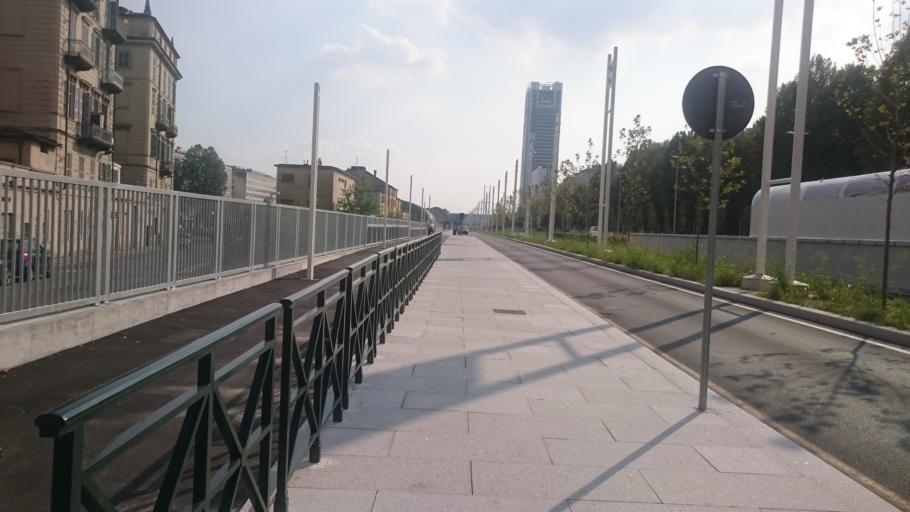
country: IT
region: Piedmont
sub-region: Provincia di Torino
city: Turin
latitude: 45.0755
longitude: 7.6683
